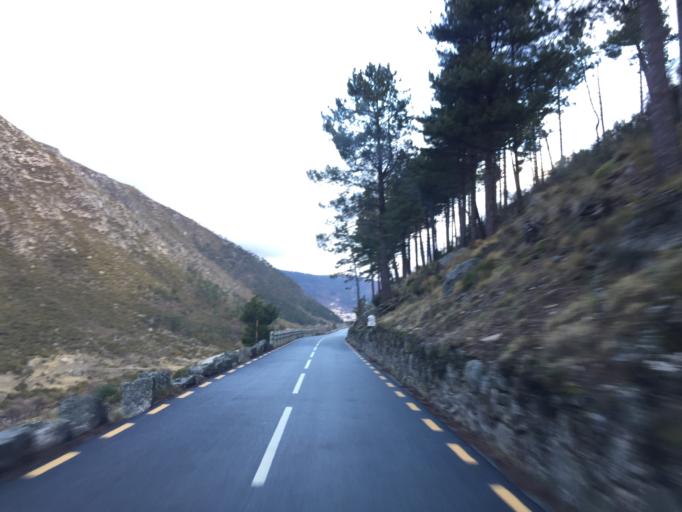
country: PT
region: Guarda
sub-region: Manteigas
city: Manteigas
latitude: 40.3522
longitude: -7.5595
